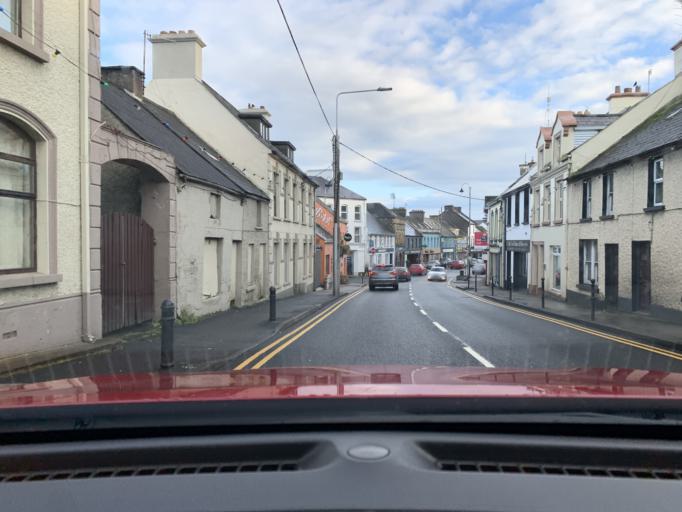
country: IE
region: Ulster
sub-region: County Donegal
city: Ballybofey
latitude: 54.7990
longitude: -7.7835
